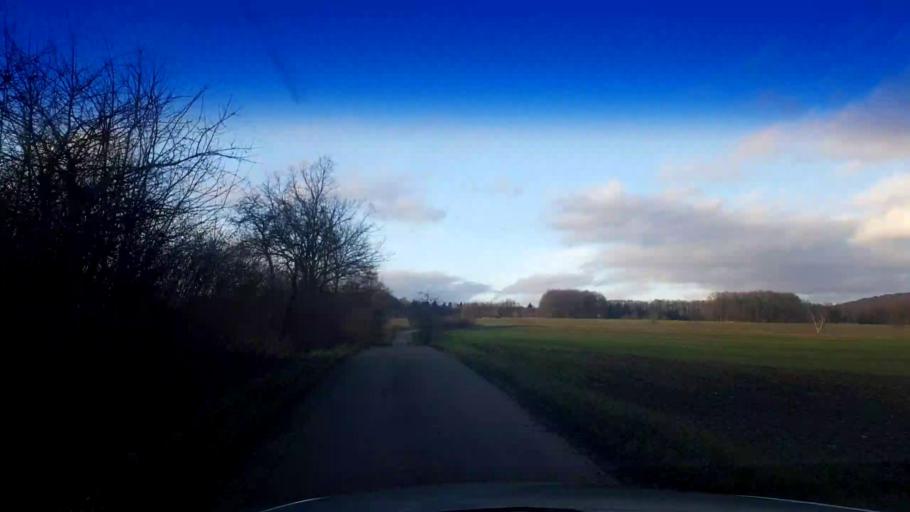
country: DE
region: Bavaria
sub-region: Upper Franconia
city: Buttenheim
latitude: 49.8130
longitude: 11.0380
